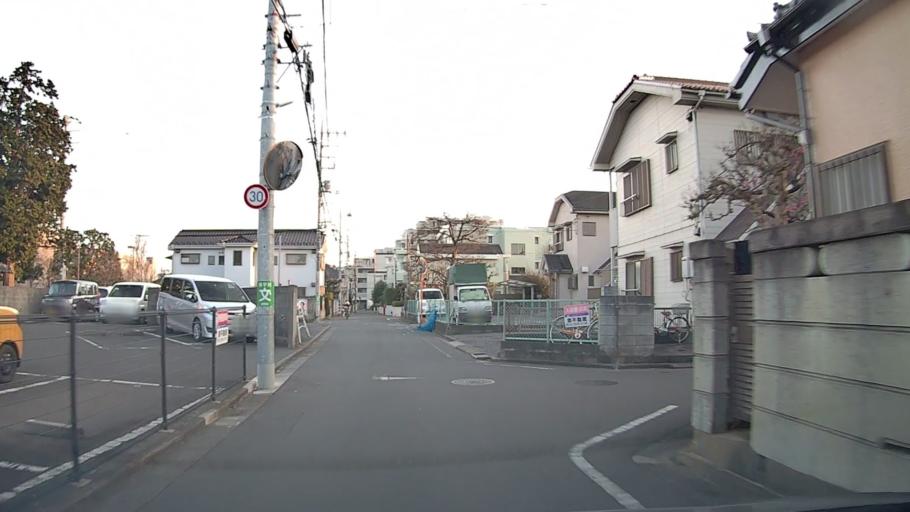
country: JP
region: Tokyo
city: Musashino
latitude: 35.7338
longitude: 139.5800
